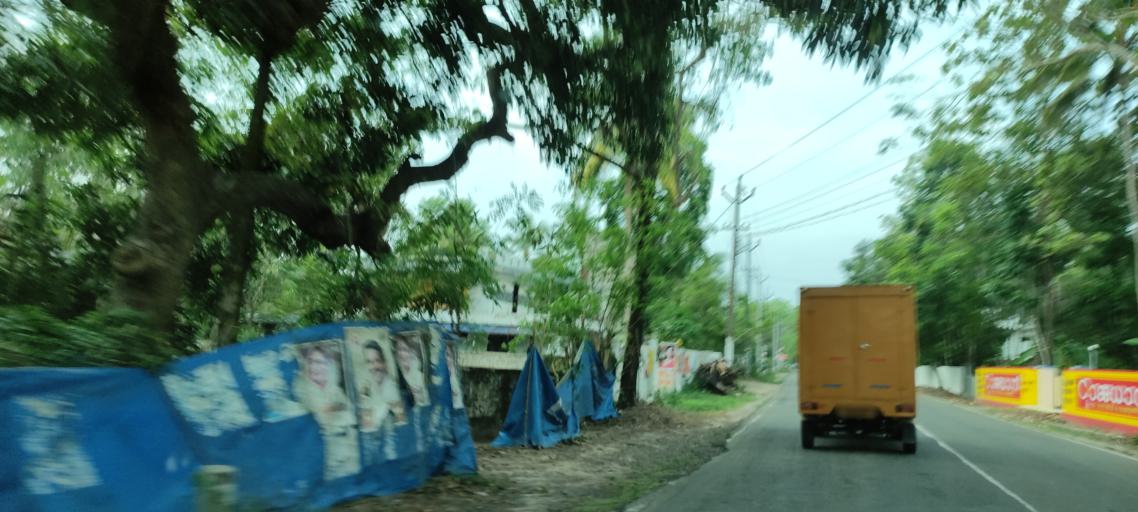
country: IN
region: Kerala
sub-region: Kottayam
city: Vaikam
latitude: 9.7581
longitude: 76.3626
